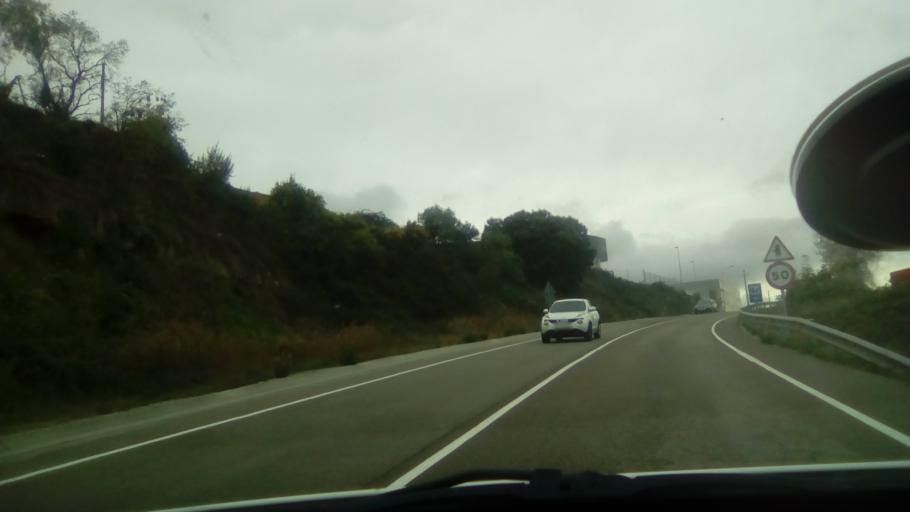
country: ES
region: Catalonia
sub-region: Provincia de Barcelona
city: Manresa
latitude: 41.7174
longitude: 1.8519
